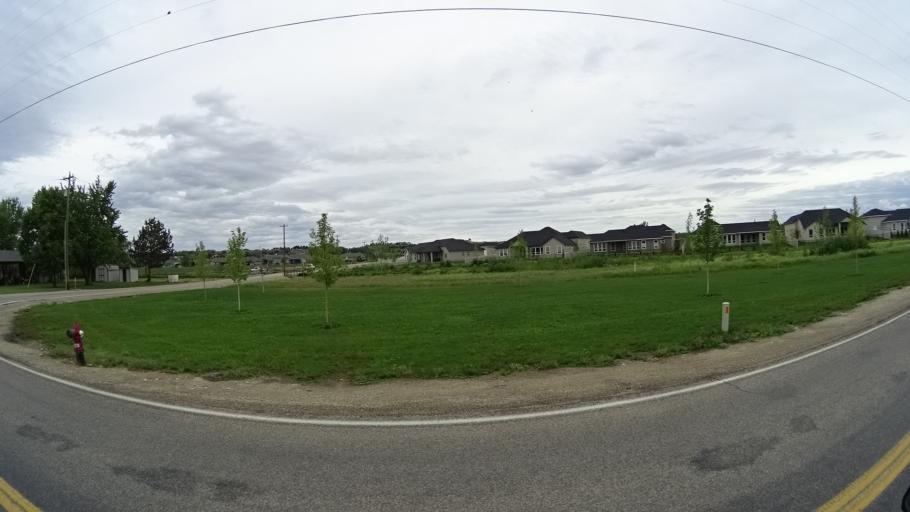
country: US
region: Idaho
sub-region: Ada County
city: Star
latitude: 43.7066
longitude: -116.5030
